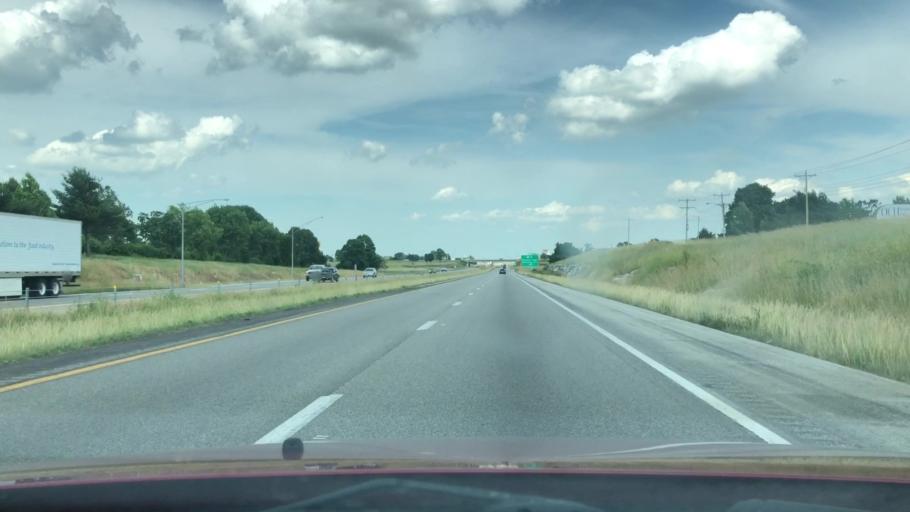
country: US
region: Missouri
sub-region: Greene County
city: Springfield
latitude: 37.2502
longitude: -93.2720
